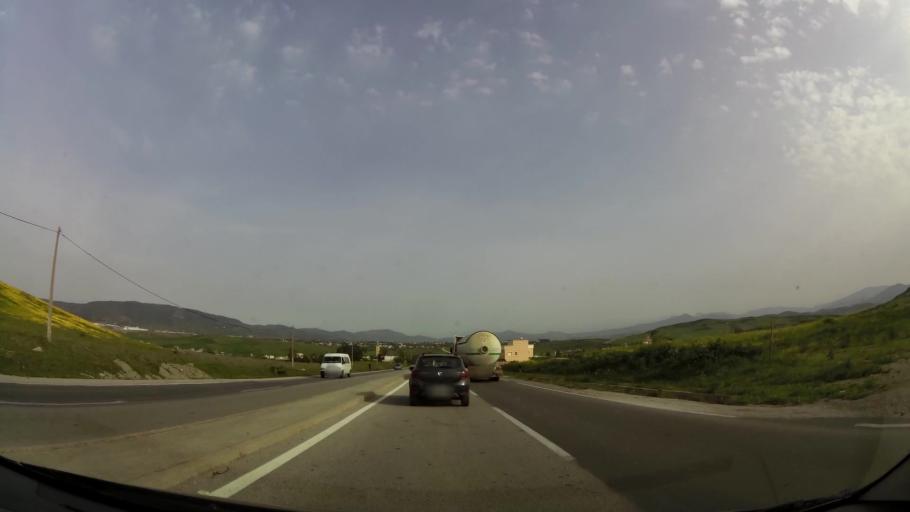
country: MA
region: Tanger-Tetouan
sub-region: Tanger-Assilah
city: Dar Chaoui
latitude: 35.6591
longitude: -5.6948
